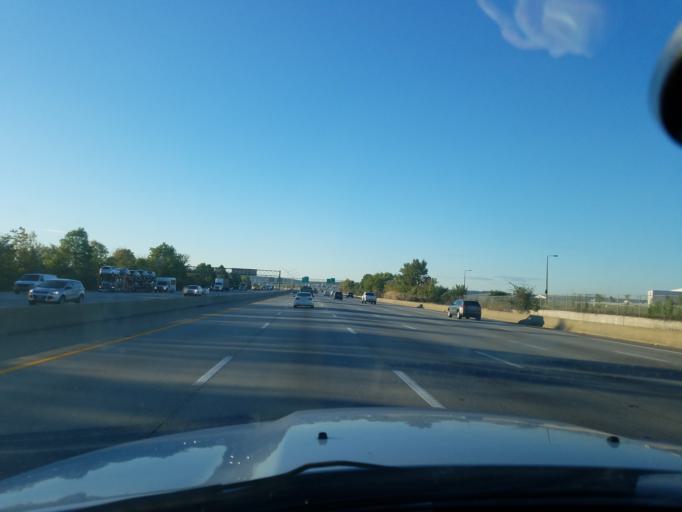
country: US
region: Kentucky
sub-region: Jefferson County
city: Audubon Park
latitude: 38.1673
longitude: -85.7206
